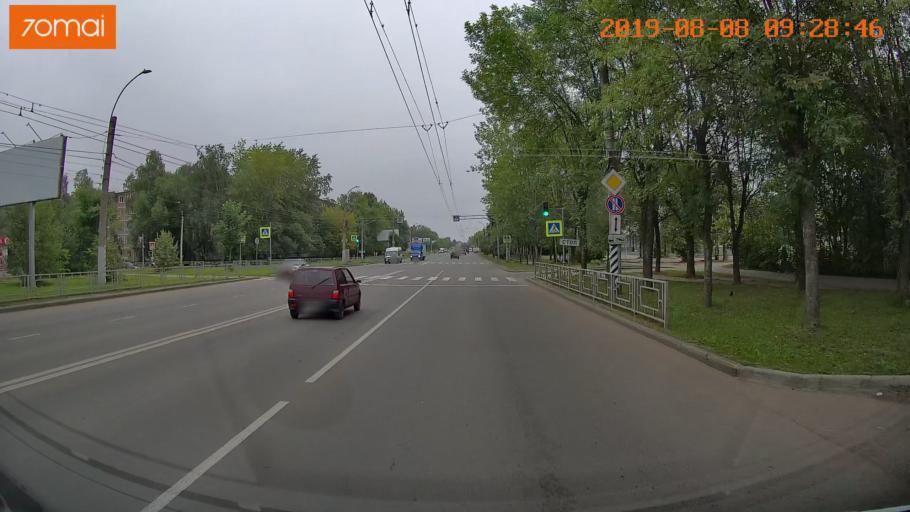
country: RU
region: Ivanovo
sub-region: Gorod Ivanovo
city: Ivanovo
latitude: 56.9665
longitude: 41.0066
